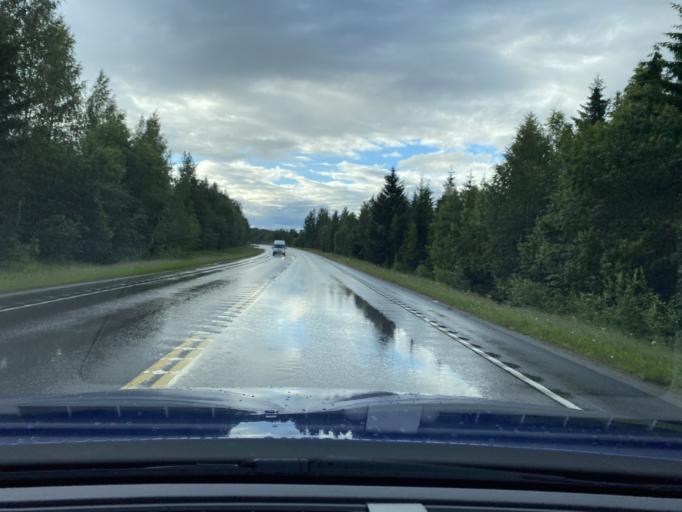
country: FI
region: Haeme
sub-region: Riihimaeki
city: Riihimaeki
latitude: 60.6654
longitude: 24.7892
